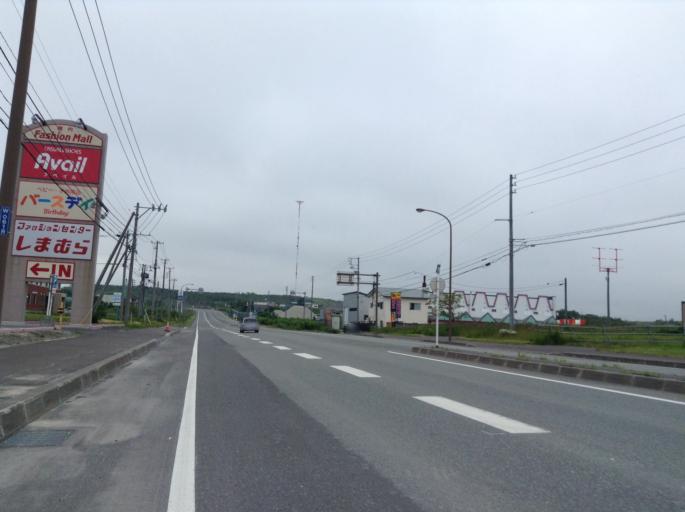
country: JP
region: Hokkaido
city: Wakkanai
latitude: 45.3802
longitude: 141.7098
